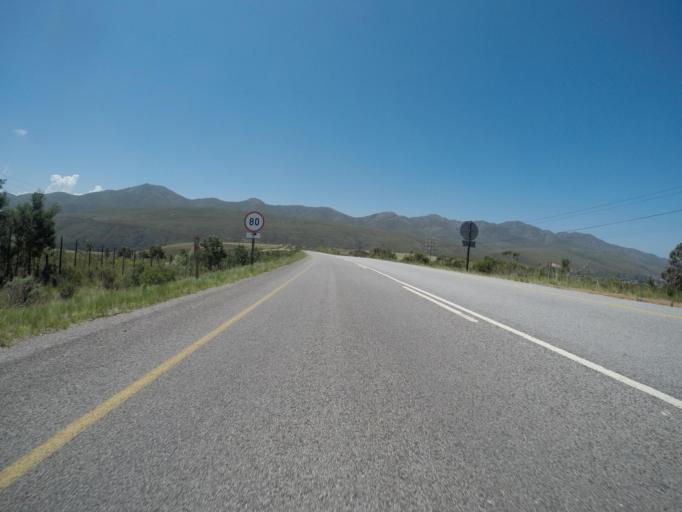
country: ZA
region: Eastern Cape
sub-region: Cacadu District Municipality
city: Kareedouw
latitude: -33.9480
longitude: 24.3037
